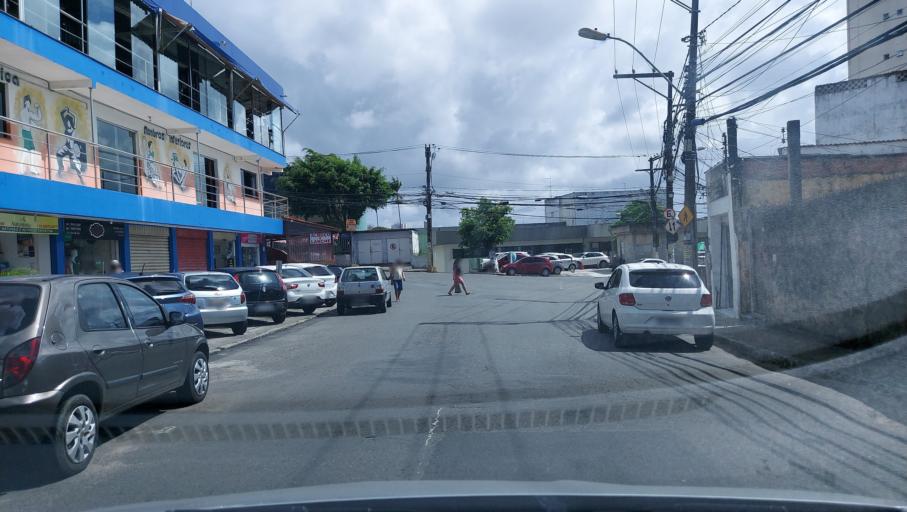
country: BR
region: Bahia
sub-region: Salvador
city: Salvador
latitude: -12.9859
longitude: -38.4773
